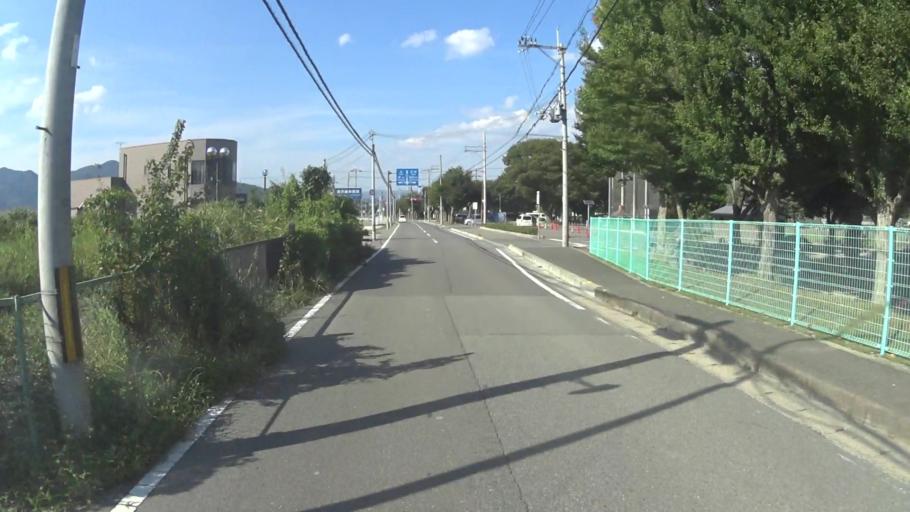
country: JP
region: Kyoto
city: Kameoka
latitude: 35.0115
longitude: 135.5481
